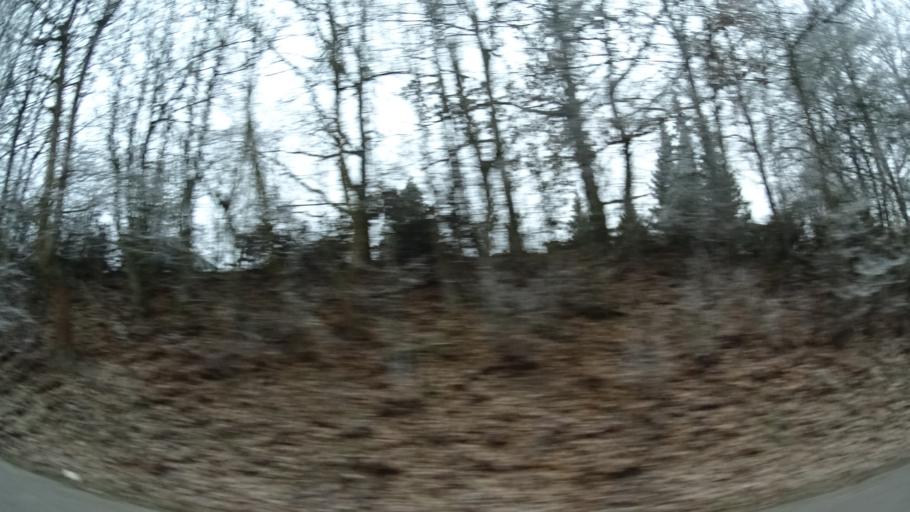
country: DE
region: Bavaria
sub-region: Regierungsbezirk Unterfranken
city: Hassfurt
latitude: 50.0495
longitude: 10.5255
